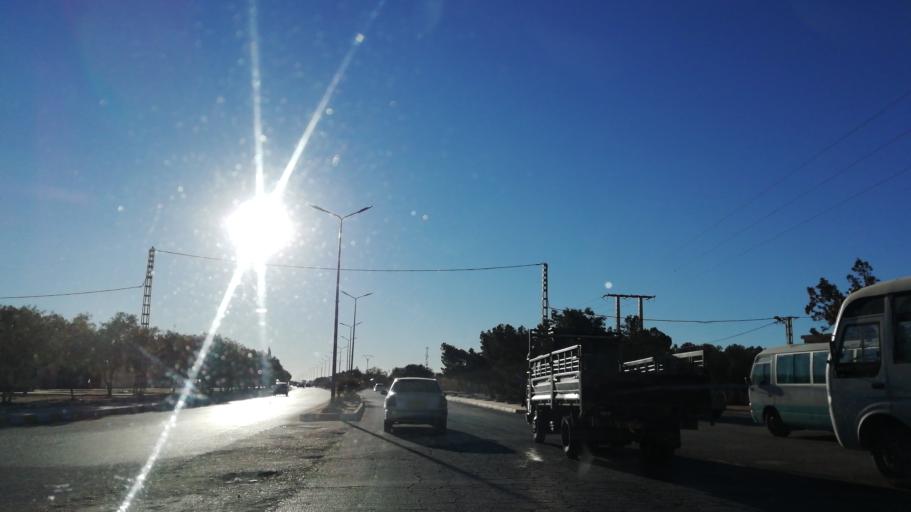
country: DZ
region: Saida
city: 'Ain el Hadjar
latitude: 34.0321
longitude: 0.0890
